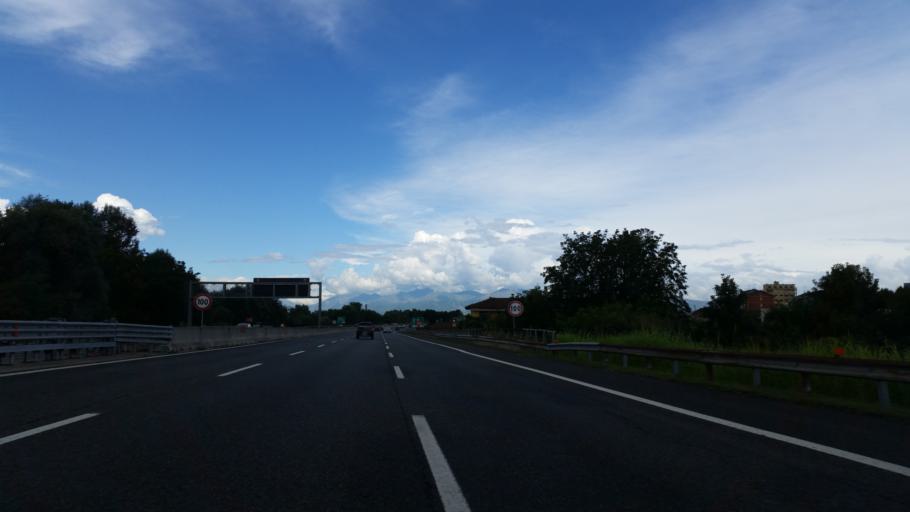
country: IT
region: Piedmont
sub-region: Provincia di Torino
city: Moncalieri
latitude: 44.9941
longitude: 7.6827
